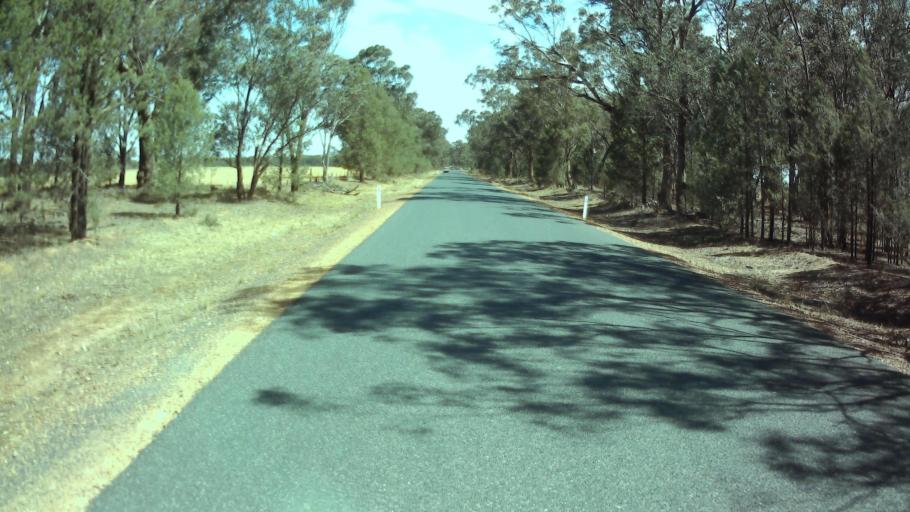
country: AU
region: New South Wales
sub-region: Weddin
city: Grenfell
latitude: -34.0338
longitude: 148.1340
